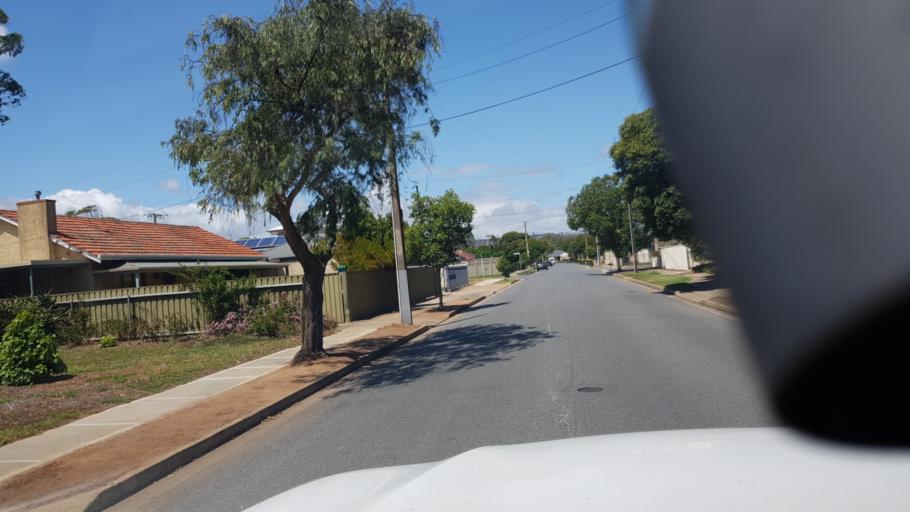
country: AU
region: South Australia
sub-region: Holdfast Bay
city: North Brighton
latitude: -35.0068
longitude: 138.5313
